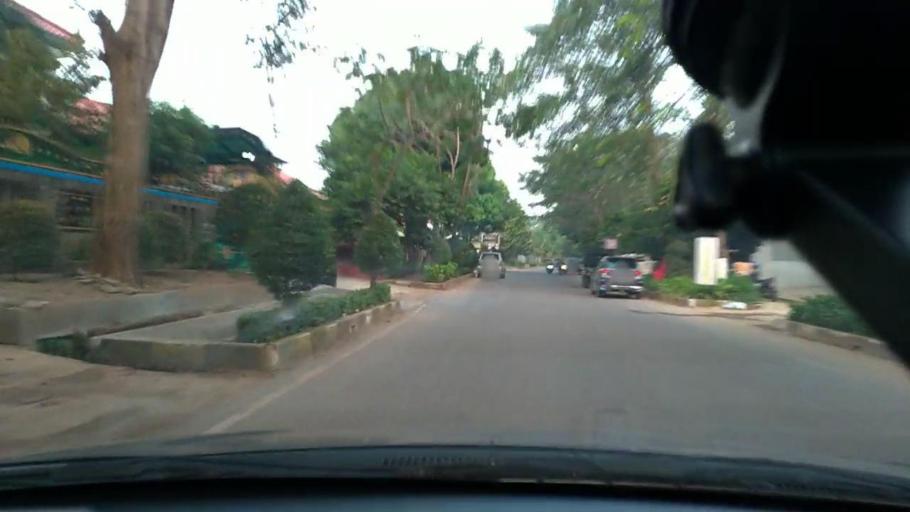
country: ID
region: West Java
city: Purwakarta
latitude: -6.5267
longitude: 107.4361
